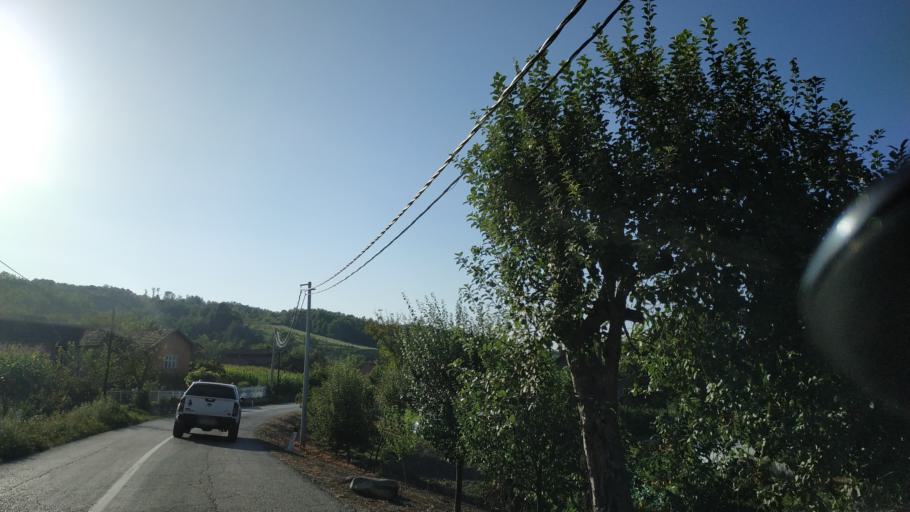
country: RS
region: Central Serbia
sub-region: Rasinski Okrug
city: Krusevac
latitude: 43.4817
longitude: 21.3528
